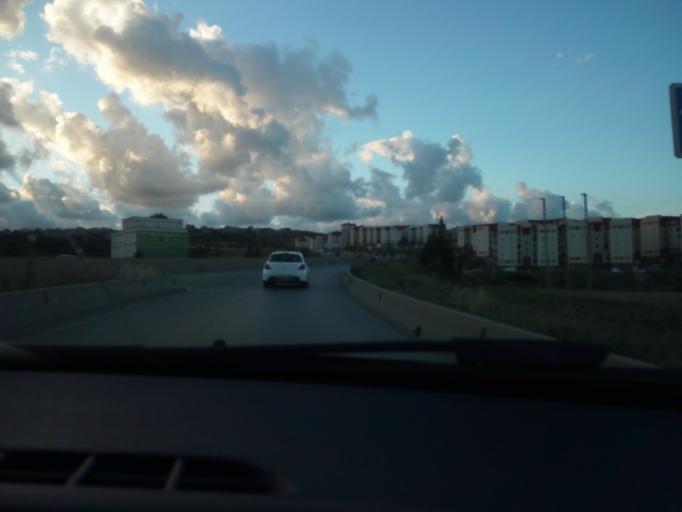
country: DZ
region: Tipaza
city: Saoula
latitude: 36.6535
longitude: 3.0117
